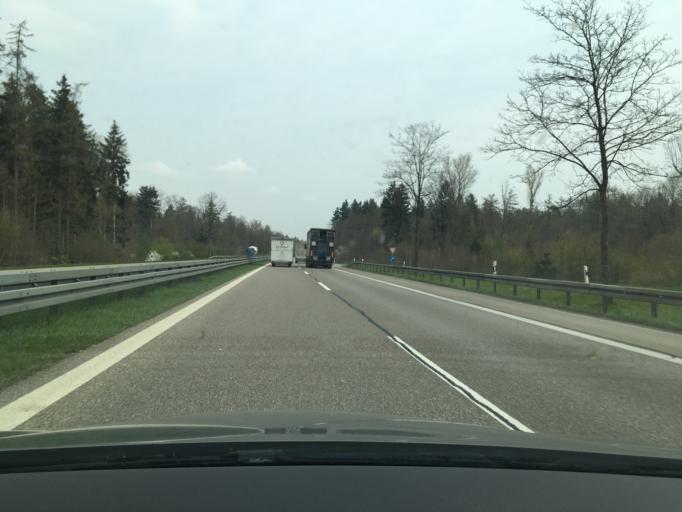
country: DE
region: Baden-Wuerttemberg
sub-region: Tuebingen Region
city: Staig
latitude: 48.3481
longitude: 9.9539
